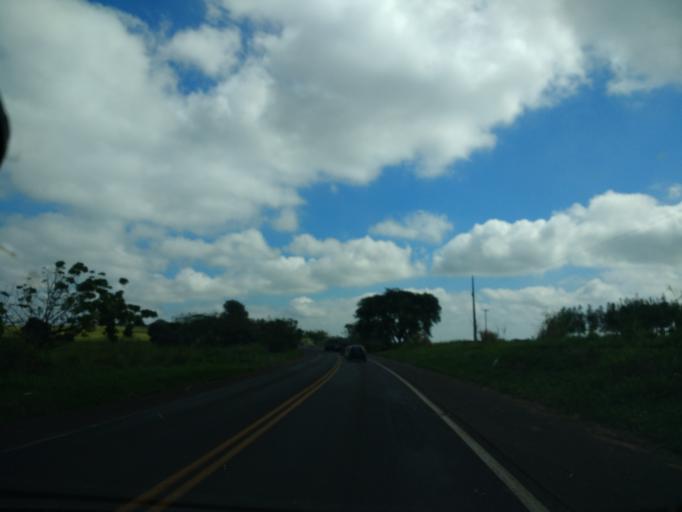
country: BR
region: Parana
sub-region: Cruzeiro Do Oeste
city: Cruzeiro do Oeste
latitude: -23.7658
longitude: -53.1174
